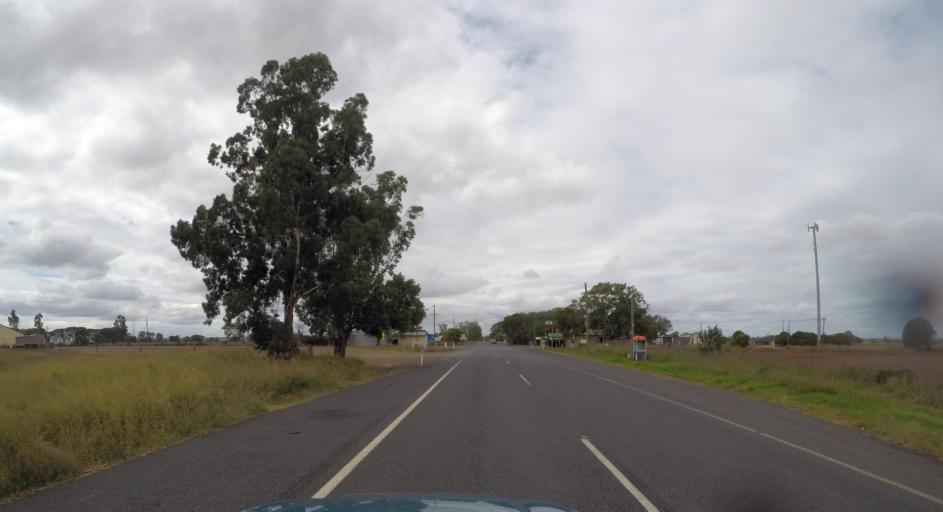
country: AU
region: Queensland
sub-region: South Burnett
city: Kingaroy
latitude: -26.3951
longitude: 151.2427
